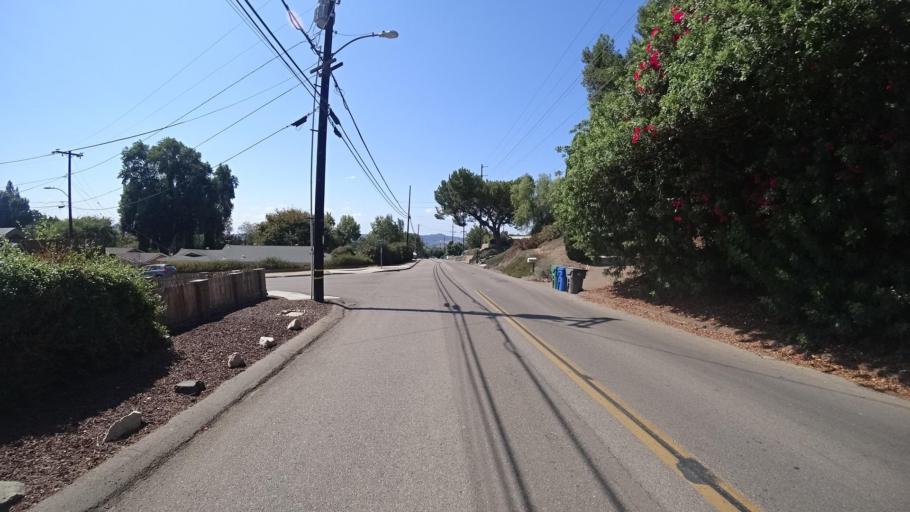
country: US
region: California
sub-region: San Diego County
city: Winter Gardens
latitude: 32.8286
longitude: -116.9226
